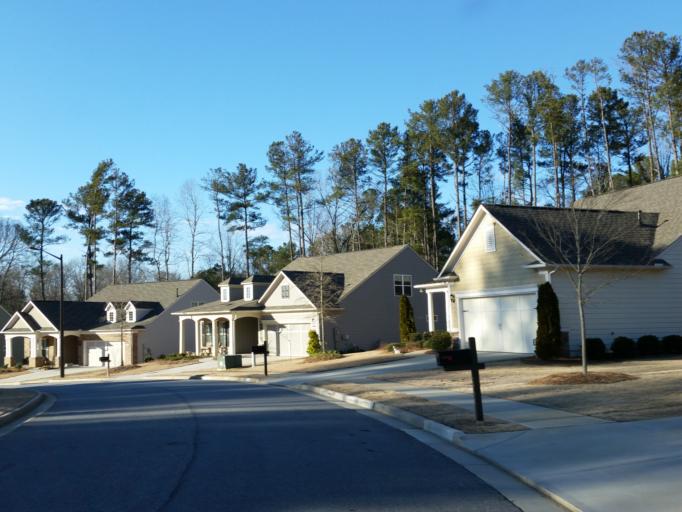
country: US
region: Georgia
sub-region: Cherokee County
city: Woodstock
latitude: 34.0231
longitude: -84.5077
